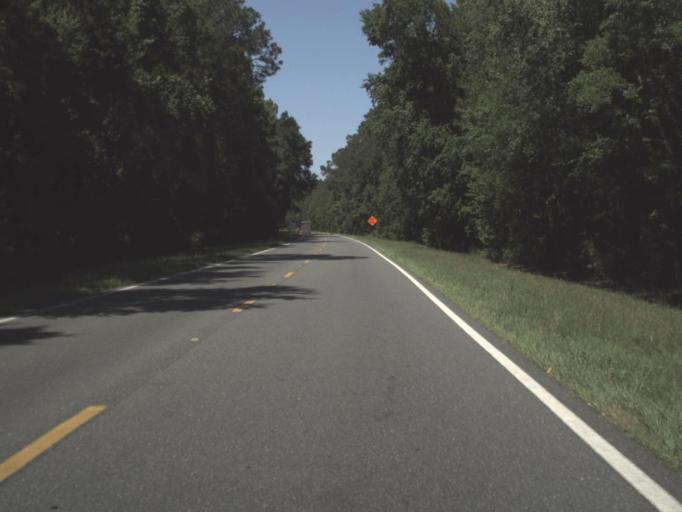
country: US
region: Florida
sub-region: Duval County
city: Baldwin
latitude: 30.3269
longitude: -81.9603
